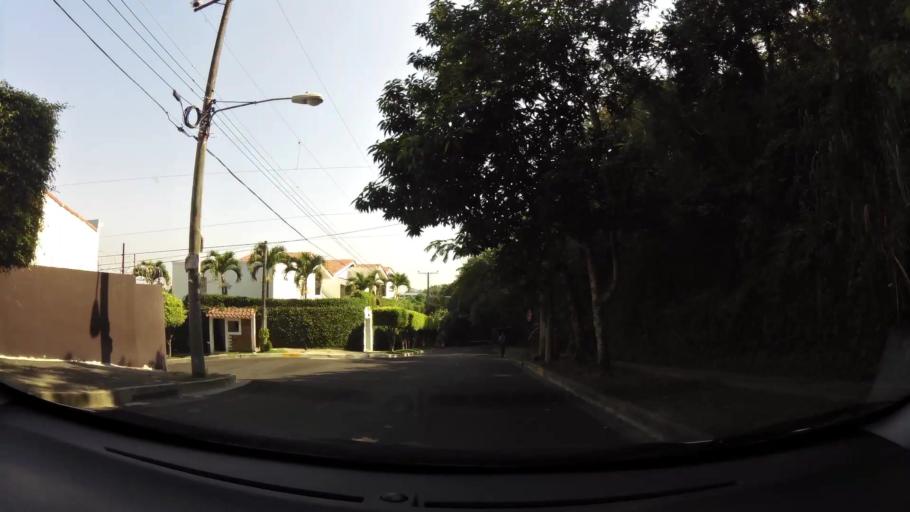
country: SV
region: La Libertad
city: Antiguo Cuscatlan
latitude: 13.6701
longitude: -89.2344
